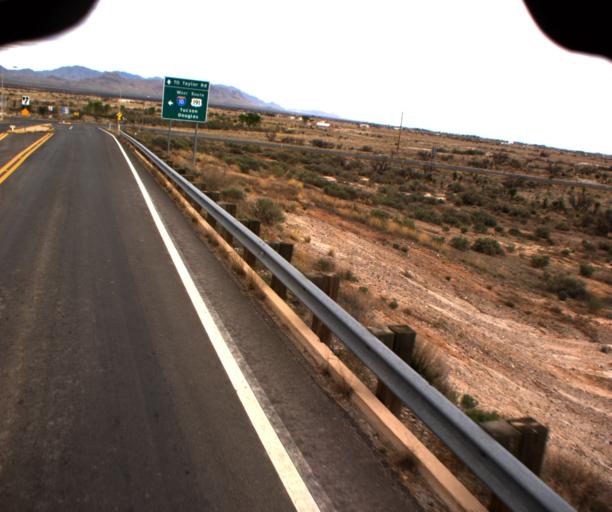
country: US
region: Arizona
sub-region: Cochise County
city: Willcox
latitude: 32.2227
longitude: -109.8785
